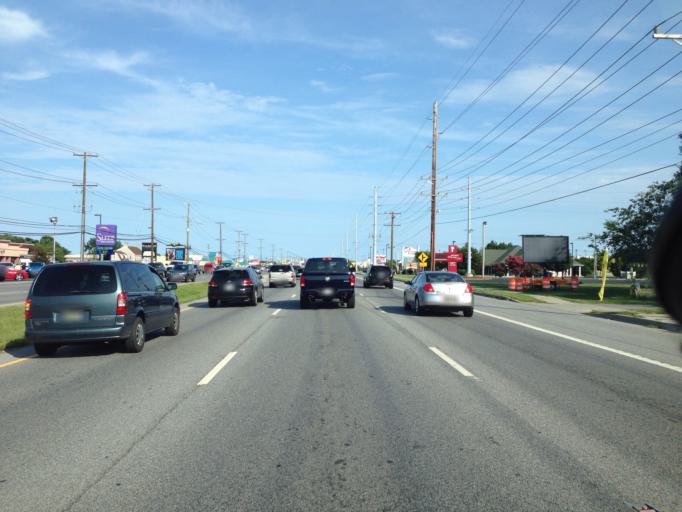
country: US
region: Delaware
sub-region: Sussex County
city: Lewes
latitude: 38.7397
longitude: -75.1459
